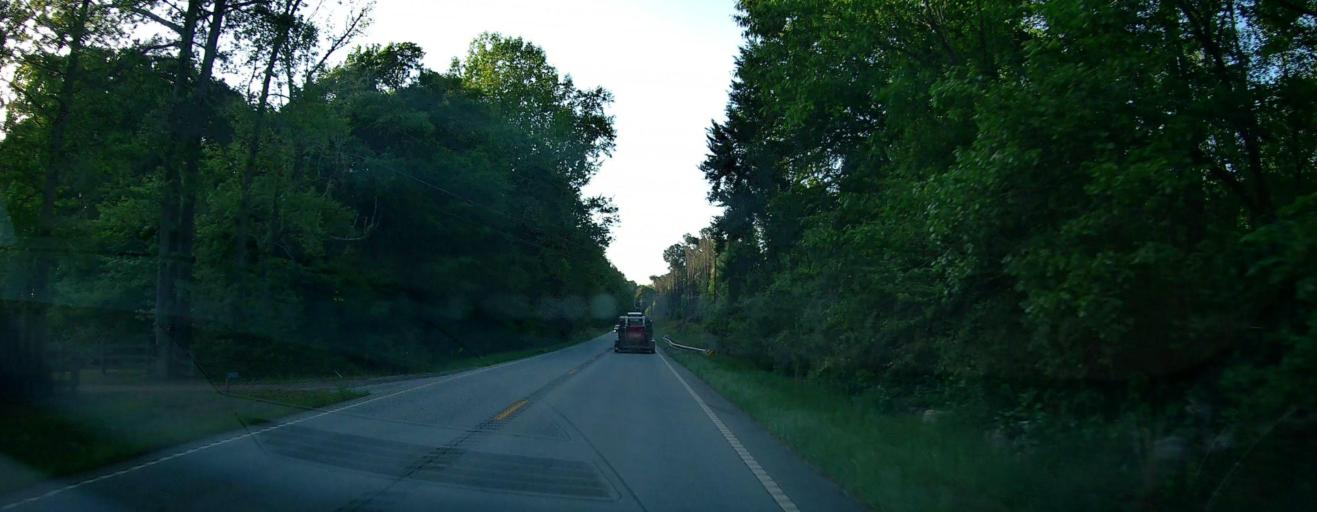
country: US
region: Georgia
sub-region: Walton County
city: Social Circle
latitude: 33.5403
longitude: -83.7257
